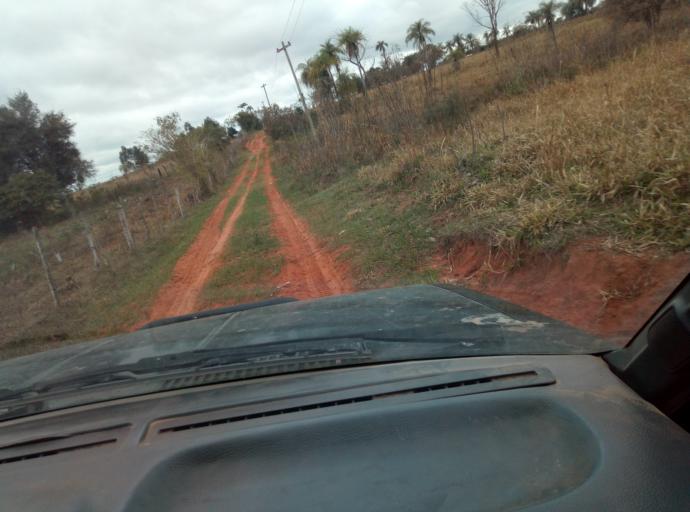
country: PY
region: Caaguazu
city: Doctor Cecilio Baez
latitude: -25.1450
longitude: -56.2942
